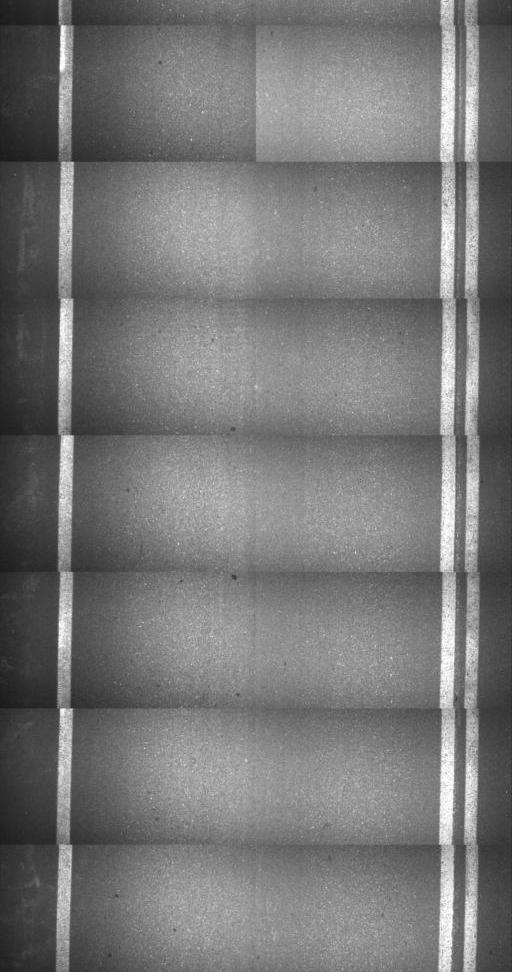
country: US
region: New Hampshire
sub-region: Coos County
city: Colebrook
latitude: 44.9865
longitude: -71.5422
